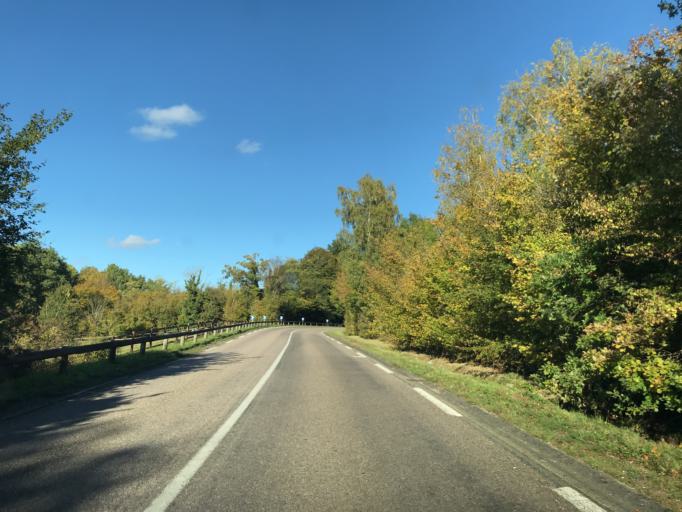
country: FR
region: Haute-Normandie
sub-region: Departement de l'Eure
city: Saint-Aubin-sur-Gaillon
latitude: 49.1071
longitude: 1.2942
